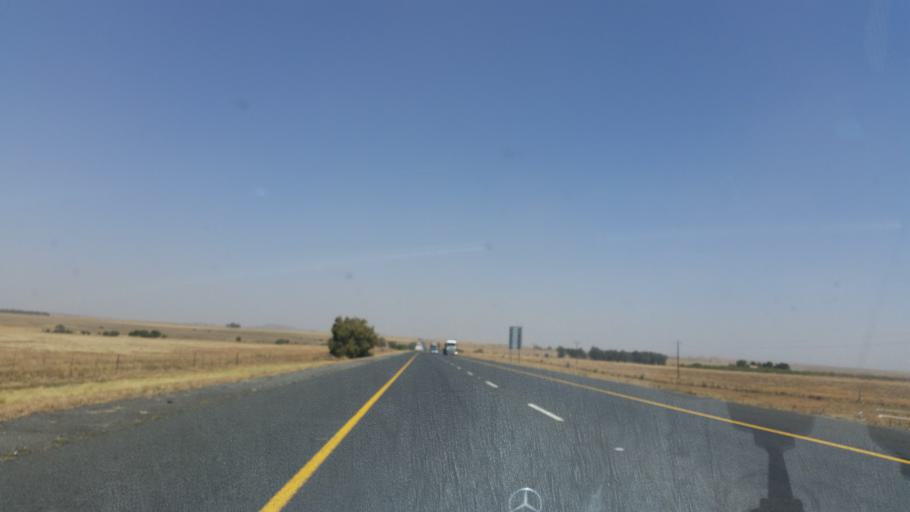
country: ZA
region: Orange Free State
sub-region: Lejweleputswa District Municipality
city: Brandfort
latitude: -28.7247
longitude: 26.7680
